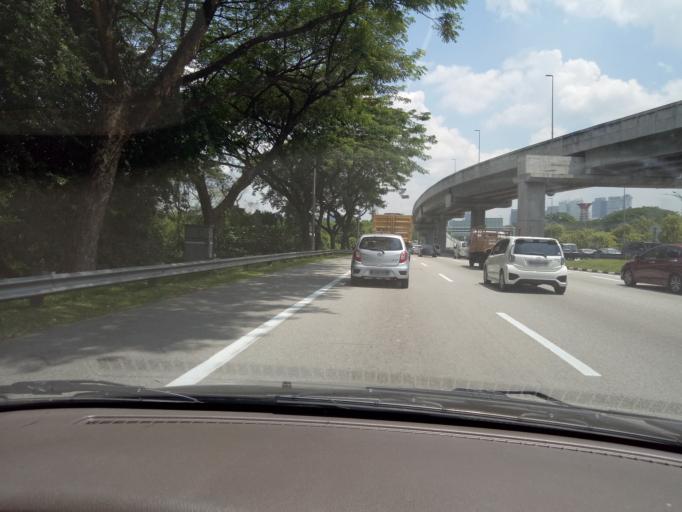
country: MY
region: Kuala Lumpur
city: Kuala Lumpur
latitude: 3.1221
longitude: 101.7067
